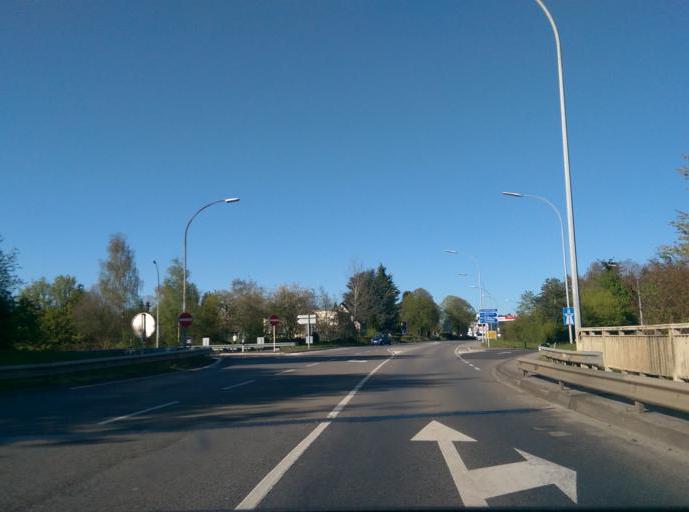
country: LU
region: Luxembourg
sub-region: Canton de Luxembourg
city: Sandweiler
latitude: 49.6428
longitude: 6.2182
